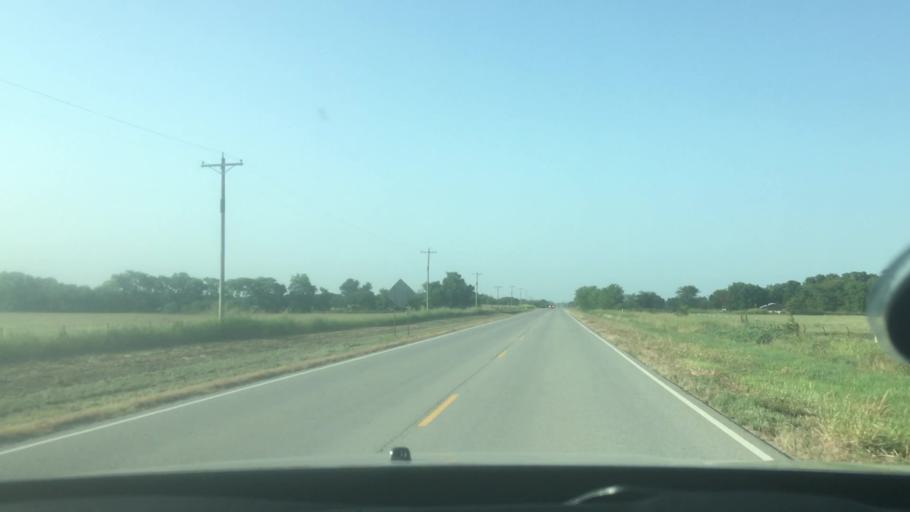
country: US
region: Oklahoma
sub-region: Coal County
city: Coalgate
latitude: 34.4246
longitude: -96.4246
